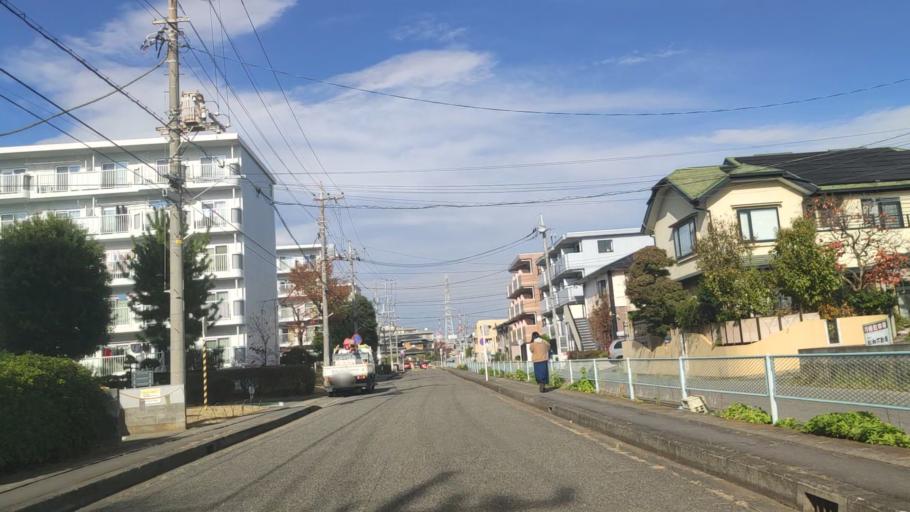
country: JP
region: Kanagawa
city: Atsugi
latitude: 35.4293
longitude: 139.3639
